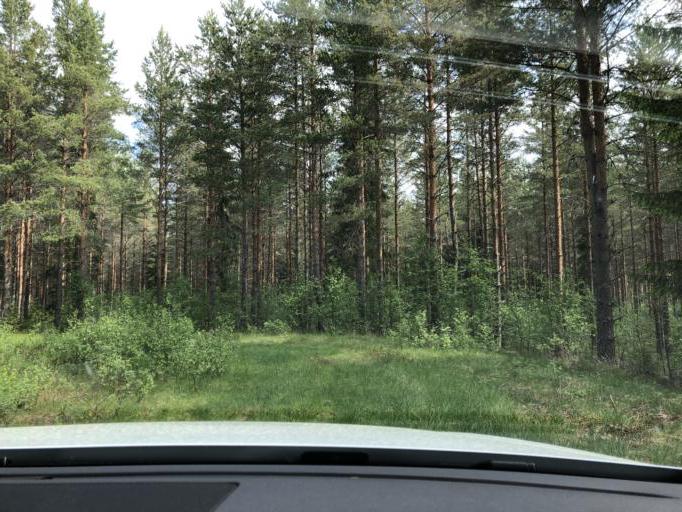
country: SE
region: Dalarna
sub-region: Avesta Kommun
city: Horndal
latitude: 60.2210
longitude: 16.5054
